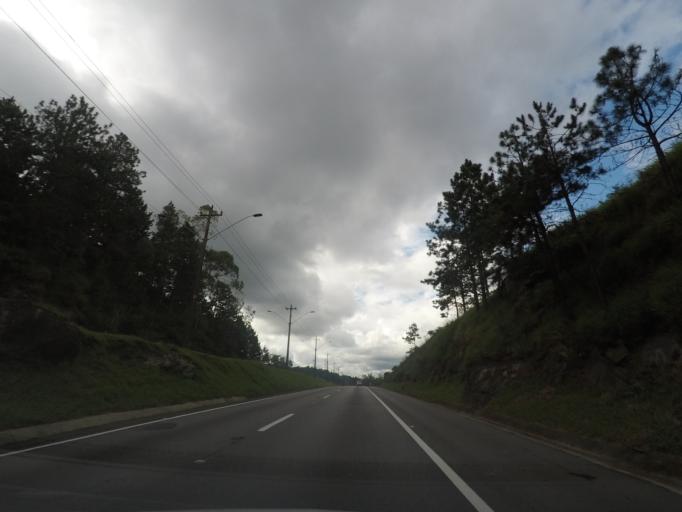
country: BR
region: Sao Paulo
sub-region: Sao Lourenco Da Serra
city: Sao Lourenco da Serra
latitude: -23.9005
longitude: -46.9889
